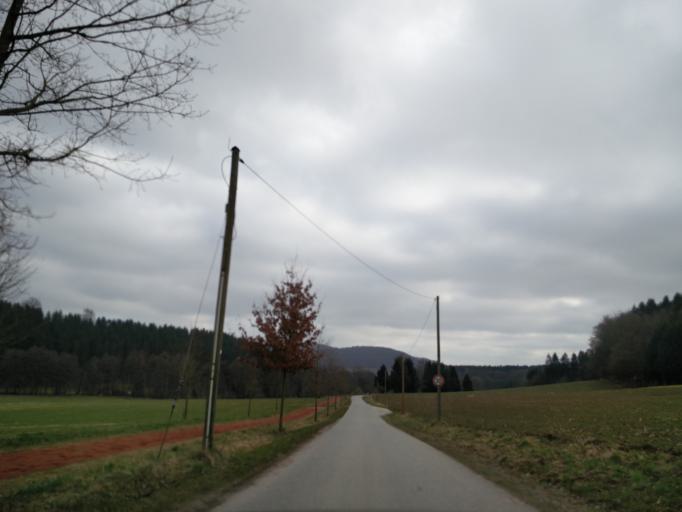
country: DE
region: North Rhine-Westphalia
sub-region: Regierungsbezirk Detmold
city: Willebadessen
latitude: 51.5283
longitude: 8.9992
